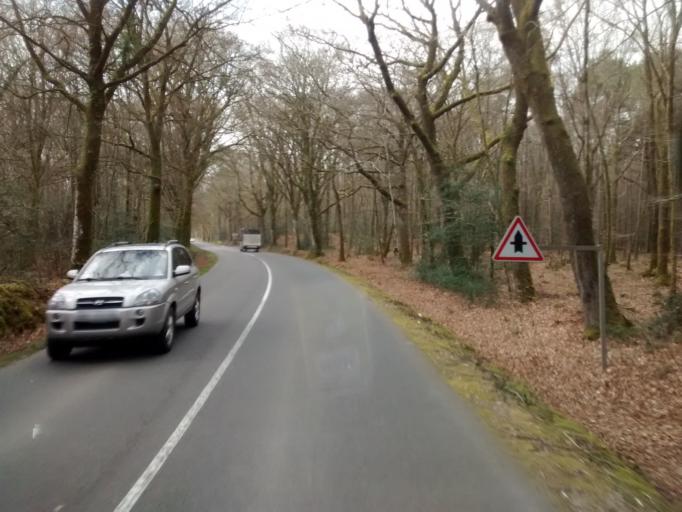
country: FR
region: Brittany
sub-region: Departement d'Ille-et-Vilaine
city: Paimpont
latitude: 48.0173
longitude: -2.1554
